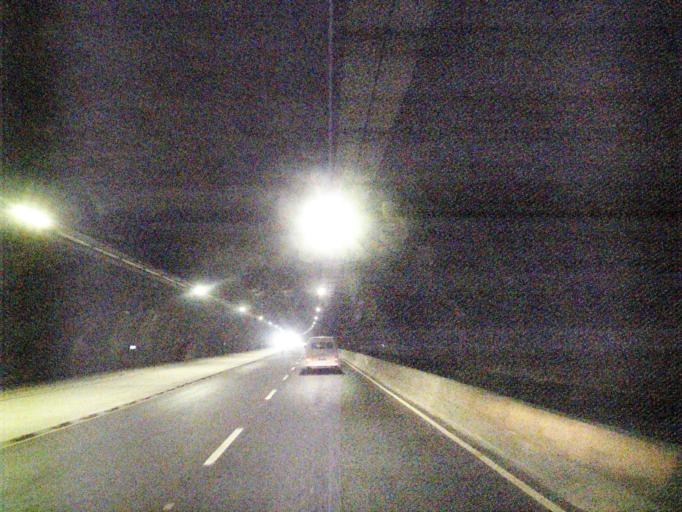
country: BR
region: Rio de Janeiro
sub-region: Niteroi
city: Niteroi
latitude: -22.9359
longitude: -43.0868
